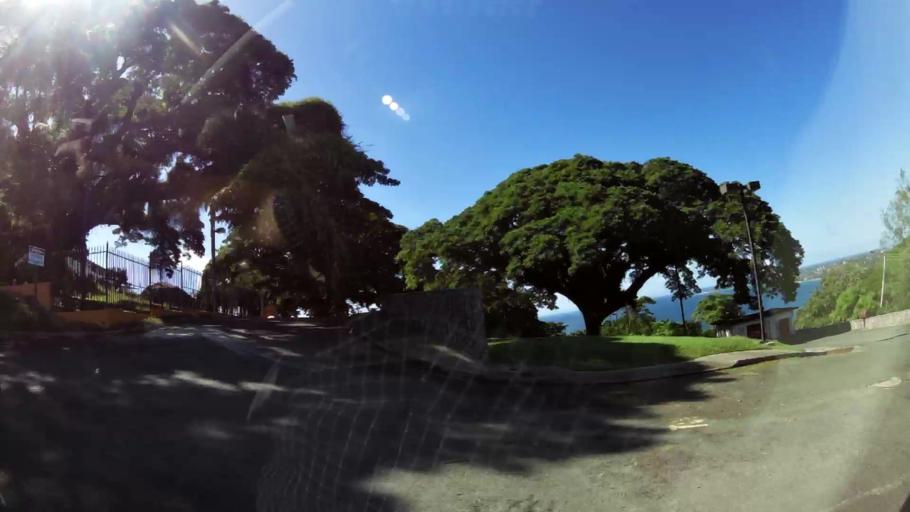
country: TT
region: Tobago
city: Scarborough
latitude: 11.1794
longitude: -60.7279
